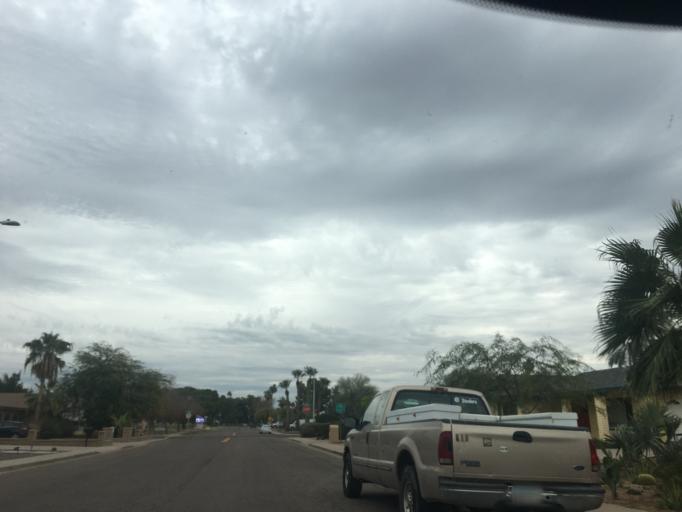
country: US
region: Arizona
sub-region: Maricopa County
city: Guadalupe
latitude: 33.3691
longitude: -111.9209
